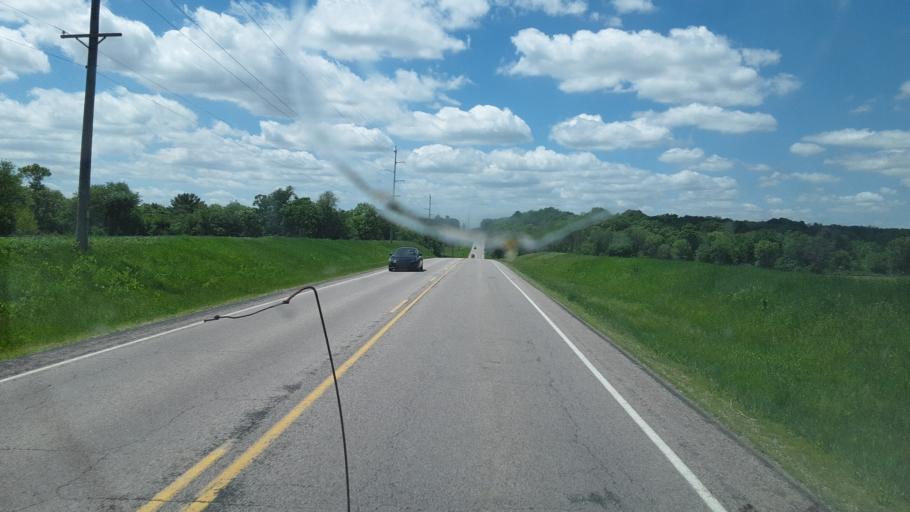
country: US
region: Wisconsin
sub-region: Sauk County
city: Lake Delton
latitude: 43.5908
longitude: -89.8528
